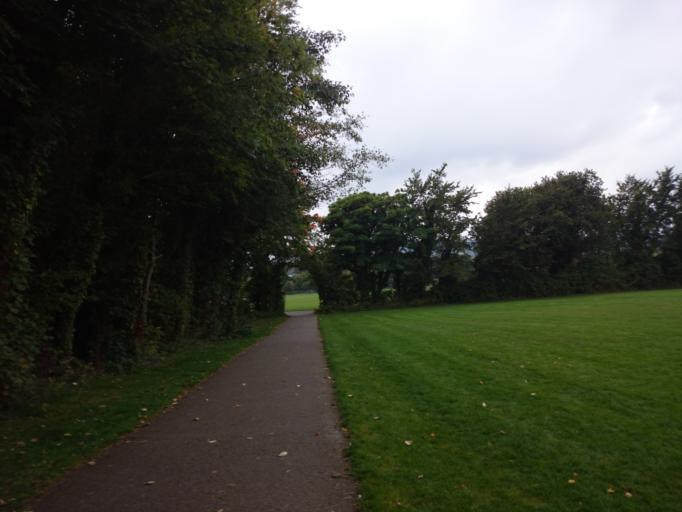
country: IE
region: Leinster
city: Shankill
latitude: 53.2237
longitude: -6.1182
